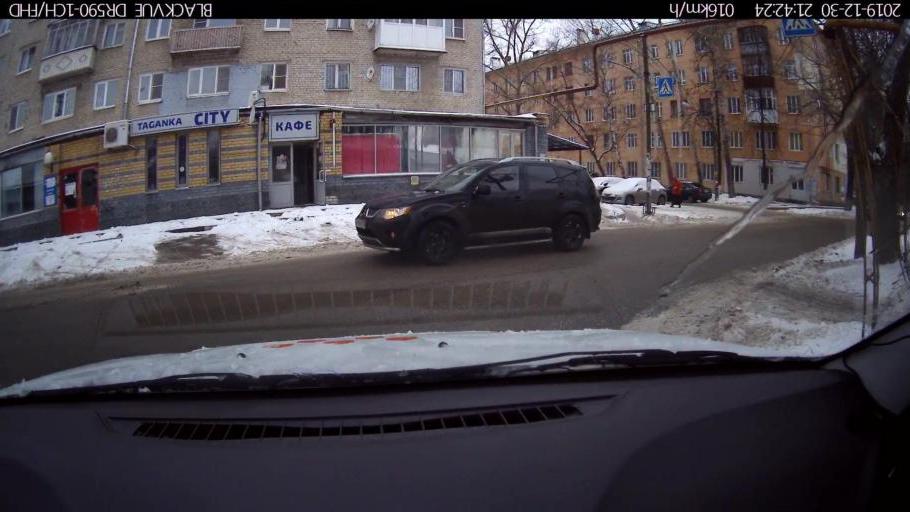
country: RU
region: Nizjnij Novgorod
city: Nizhniy Novgorod
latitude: 56.2738
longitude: 43.9244
